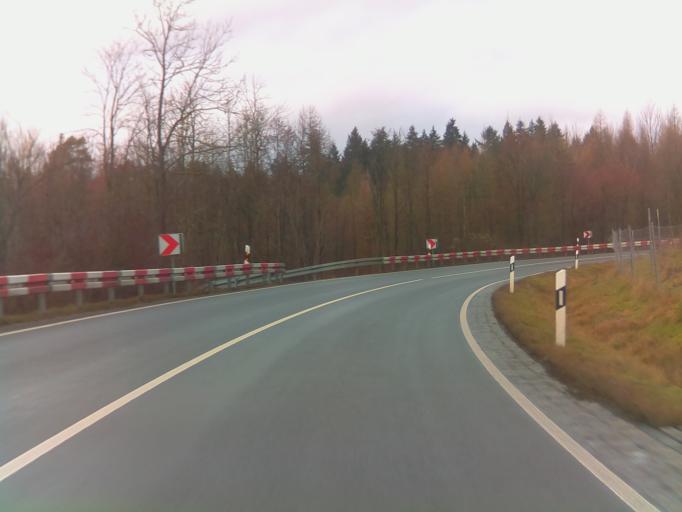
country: DE
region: Thuringia
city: Meiningen
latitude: 50.5709
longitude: 10.4445
